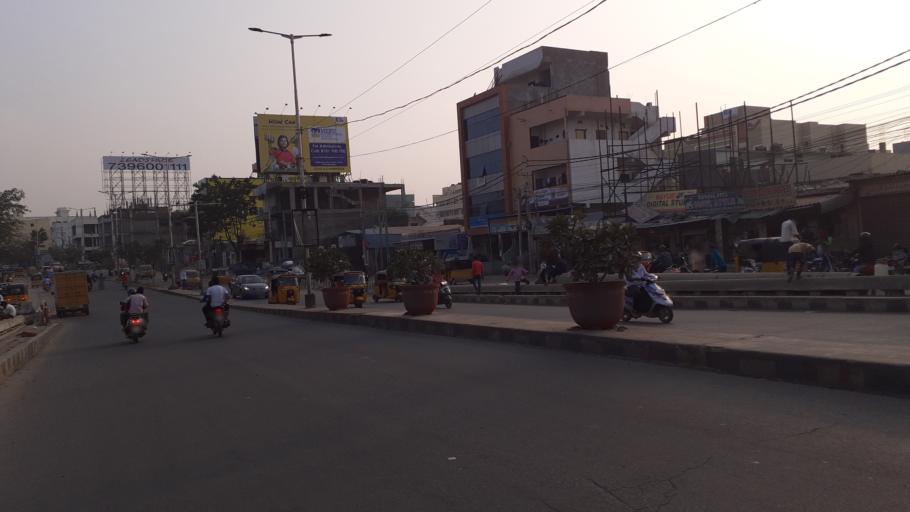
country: IN
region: Telangana
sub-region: Rangareddi
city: Kukatpalli
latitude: 17.4808
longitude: 78.3610
